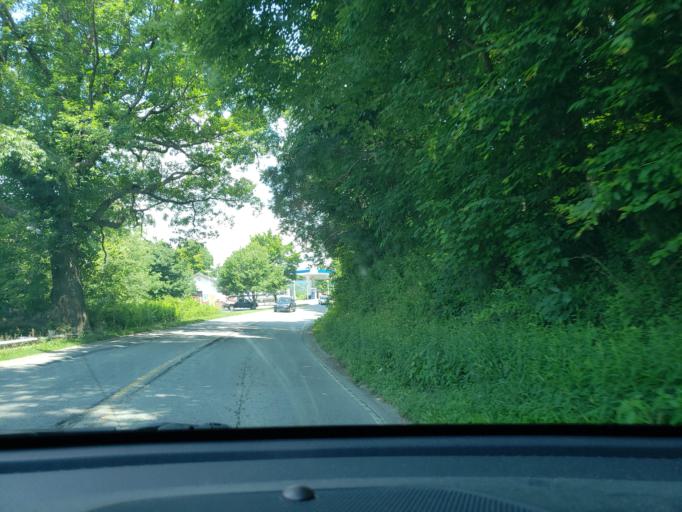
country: US
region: North Carolina
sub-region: Watauga County
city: Boone
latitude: 36.2196
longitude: -81.6386
